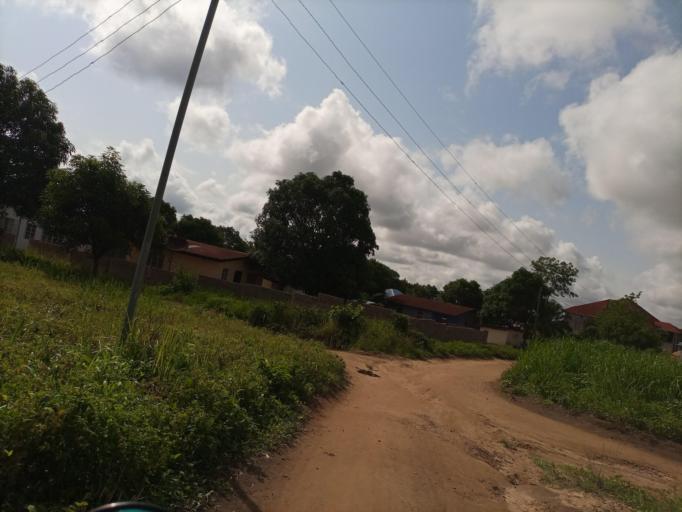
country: SL
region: Southern Province
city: Bo
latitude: 7.9619
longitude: -11.7649
